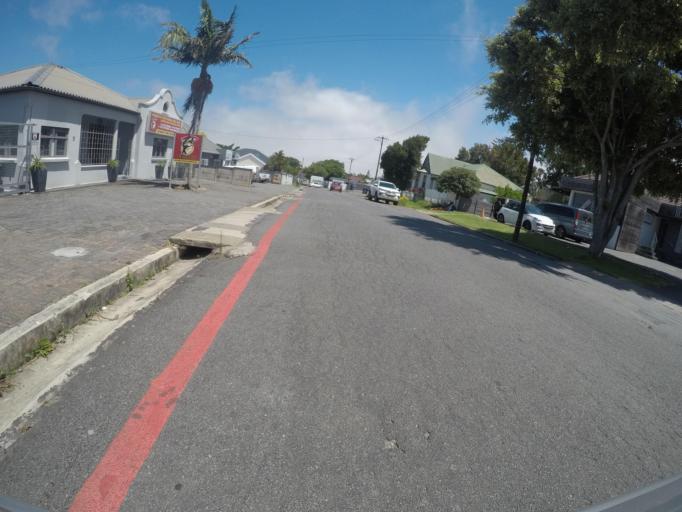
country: ZA
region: Eastern Cape
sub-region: Buffalo City Metropolitan Municipality
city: East London
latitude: -32.9852
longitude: 27.9011
